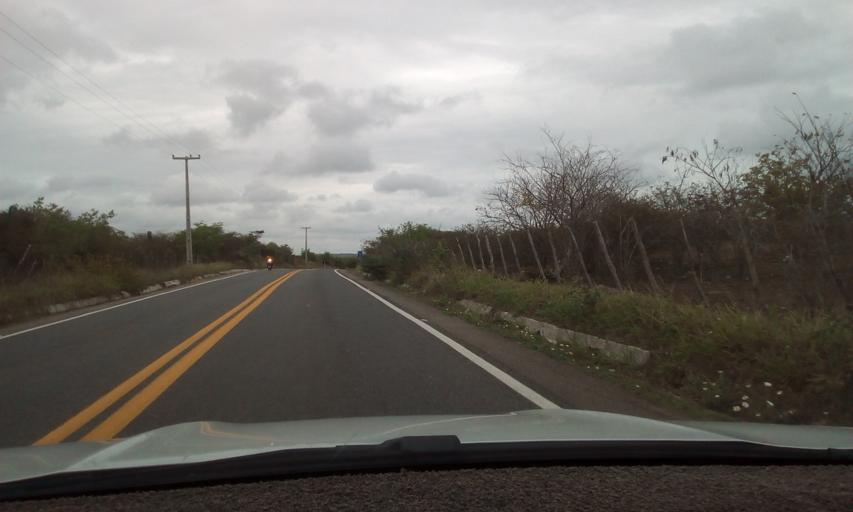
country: BR
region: Paraiba
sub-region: Areia
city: Remigio
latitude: -6.9550
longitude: -35.8122
